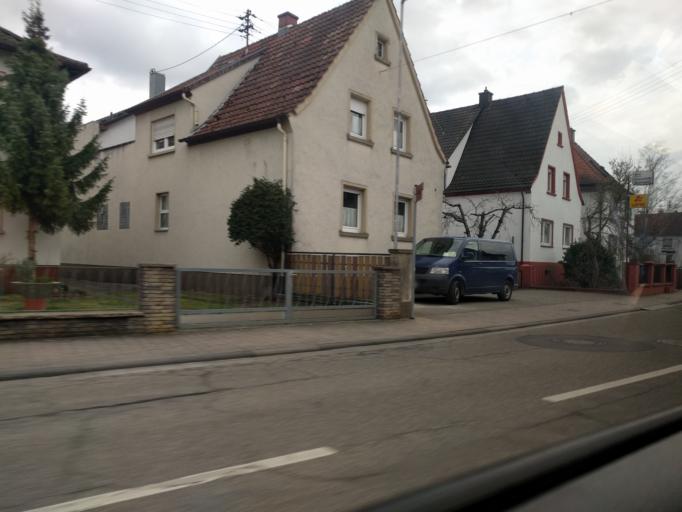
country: DE
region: Rheinland-Pfalz
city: Leimersheim
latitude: 49.1255
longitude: 8.3480
